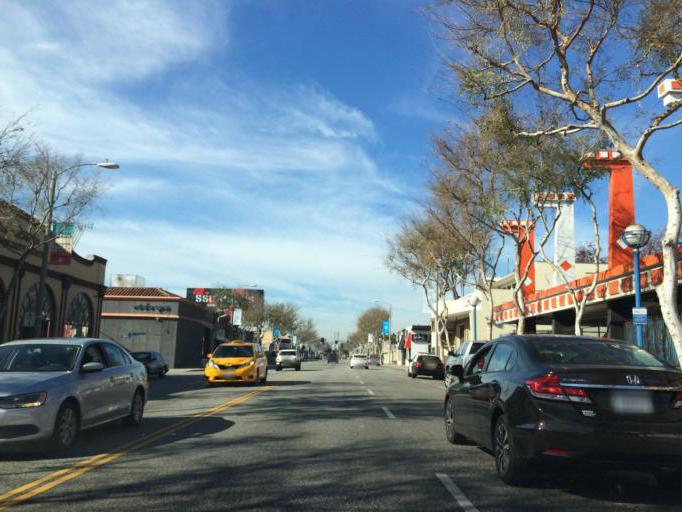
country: US
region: California
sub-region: Los Angeles County
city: West Hollywood
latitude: 34.0909
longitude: -118.3558
